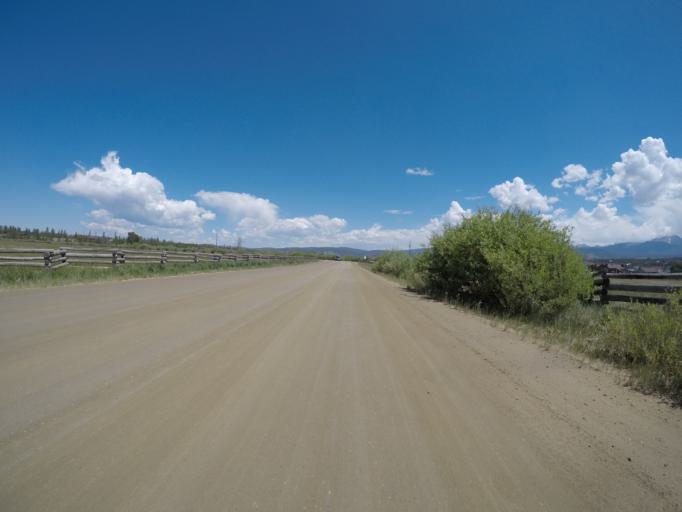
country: US
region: Colorado
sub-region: Grand County
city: Fraser
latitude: 39.9435
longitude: -105.8230
